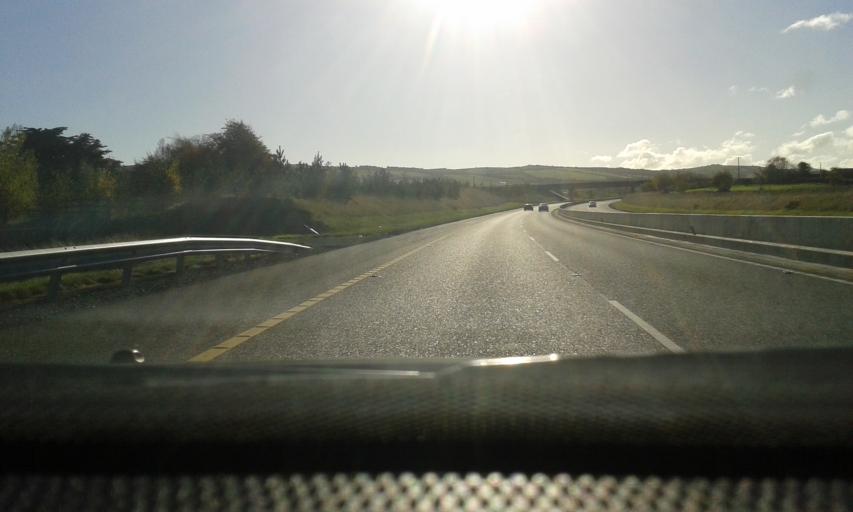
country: IE
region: Leinster
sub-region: Laois
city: Rathdowney
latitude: 52.8181
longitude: -7.4935
